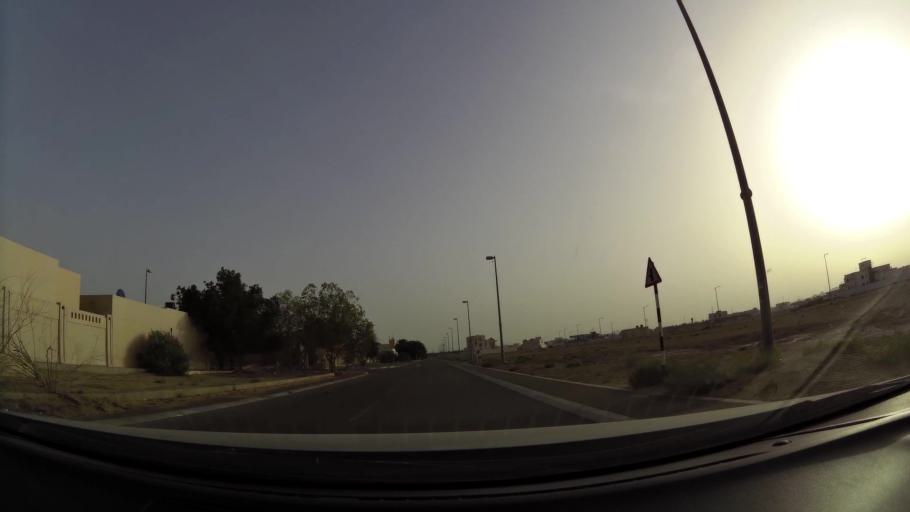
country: AE
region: Abu Dhabi
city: Al Ain
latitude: 24.1047
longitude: 55.7100
